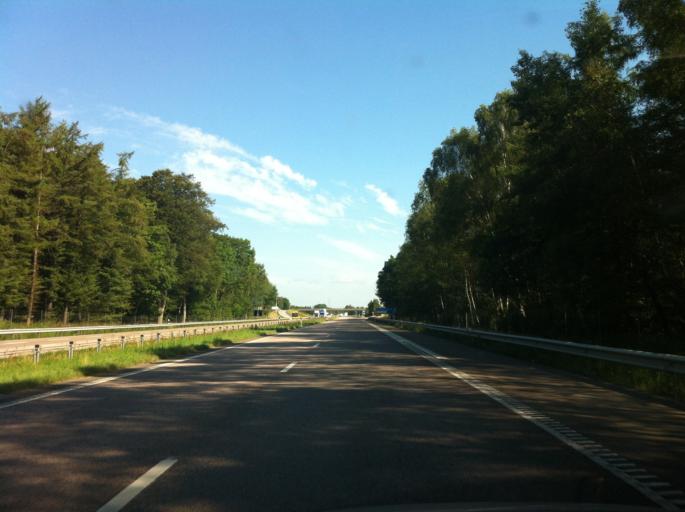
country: SE
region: Skane
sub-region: Helsingborg
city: Odakra
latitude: 56.0601
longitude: 12.7828
